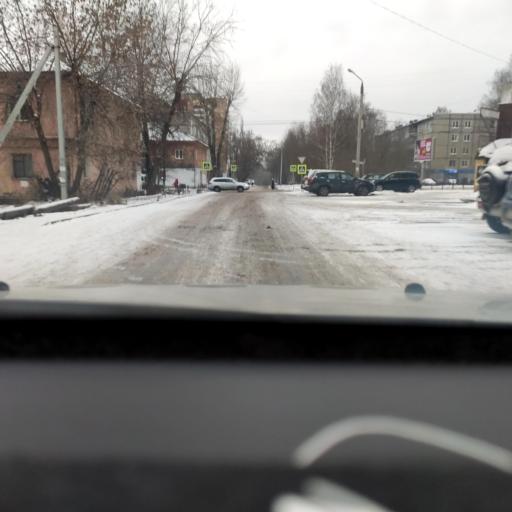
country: RU
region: Perm
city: Perm
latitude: 58.1076
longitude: 56.3784
